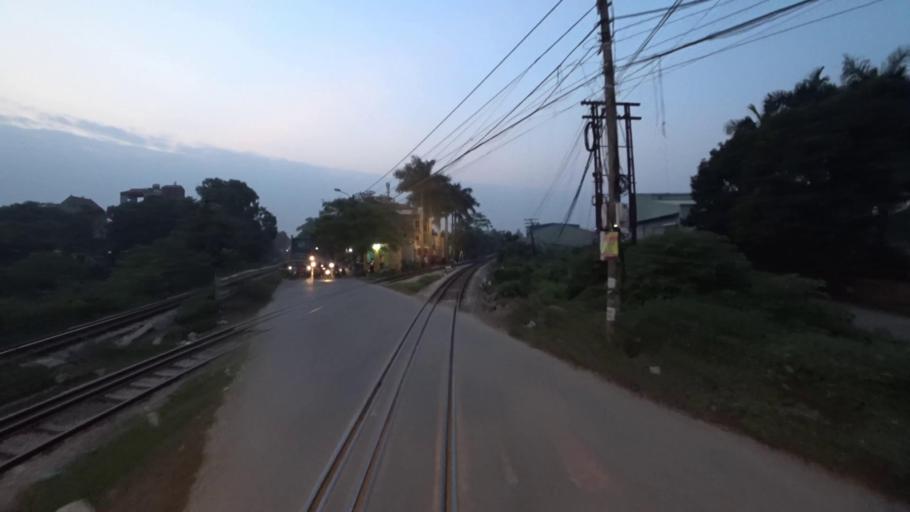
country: VN
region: Ha Noi
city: Soc Son
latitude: 21.2463
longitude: 105.8616
